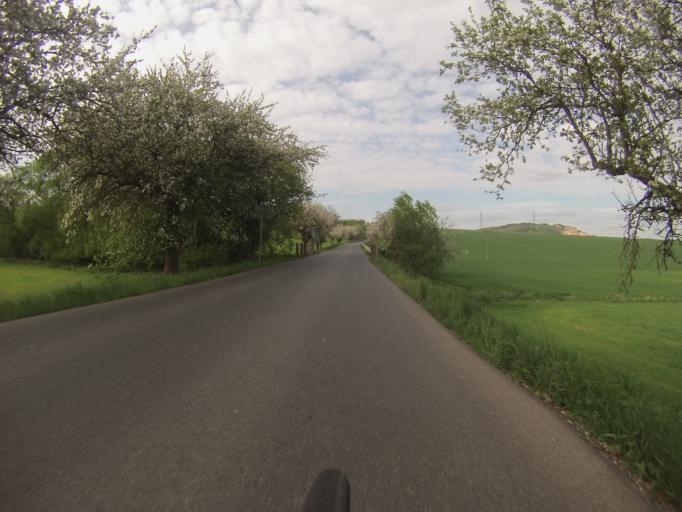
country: CZ
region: South Moravian
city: Cebin
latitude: 49.3052
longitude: 16.4607
